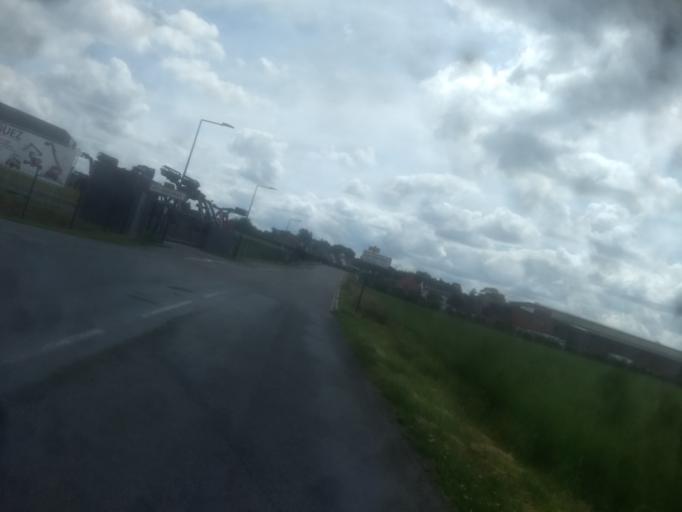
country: FR
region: Nord-Pas-de-Calais
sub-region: Departement du Pas-de-Calais
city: Mont-Saint-Eloi
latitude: 50.3358
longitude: 2.6437
